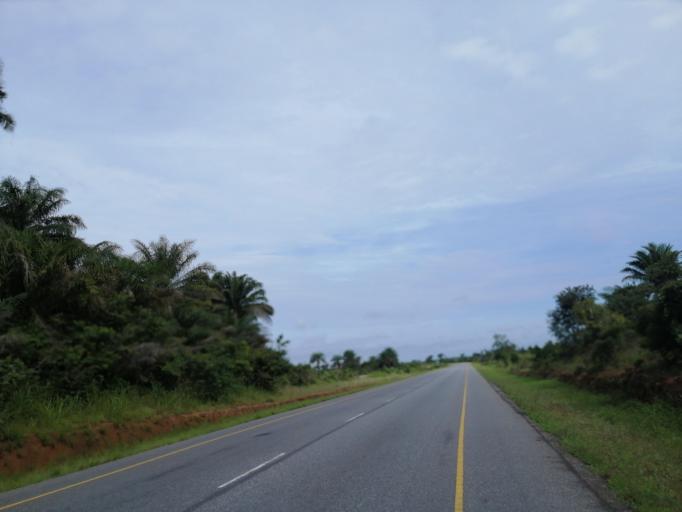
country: SL
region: Northern Province
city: Port Loko
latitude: 8.7676
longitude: -12.8919
